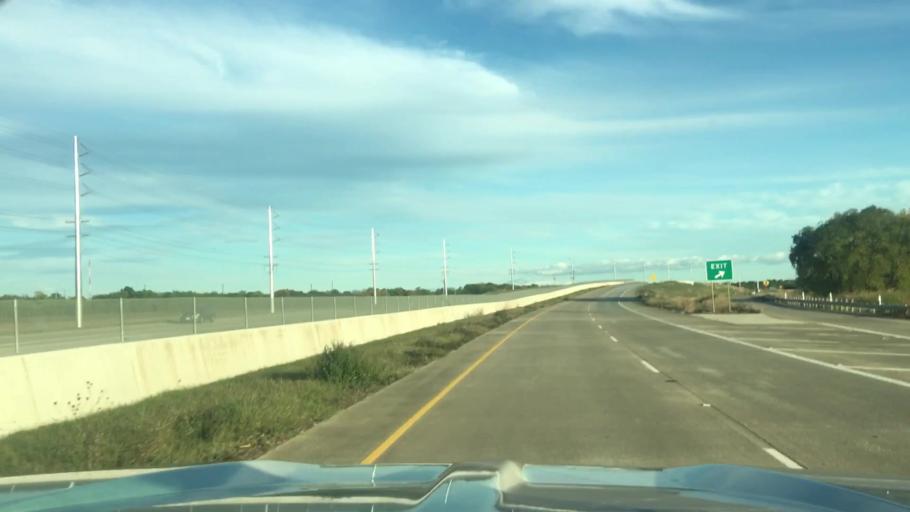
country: US
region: Texas
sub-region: Denton County
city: Denton
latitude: 33.2595
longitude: -97.1141
